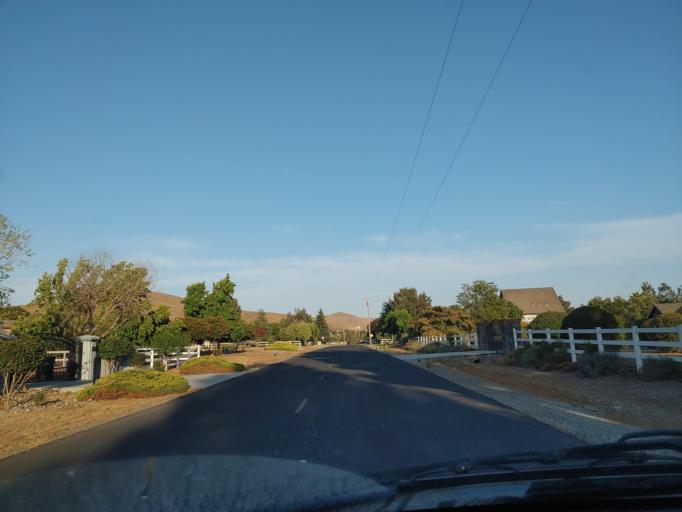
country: US
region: California
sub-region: San Benito County
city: Ridgemark
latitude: 36.7995
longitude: -121.3315
